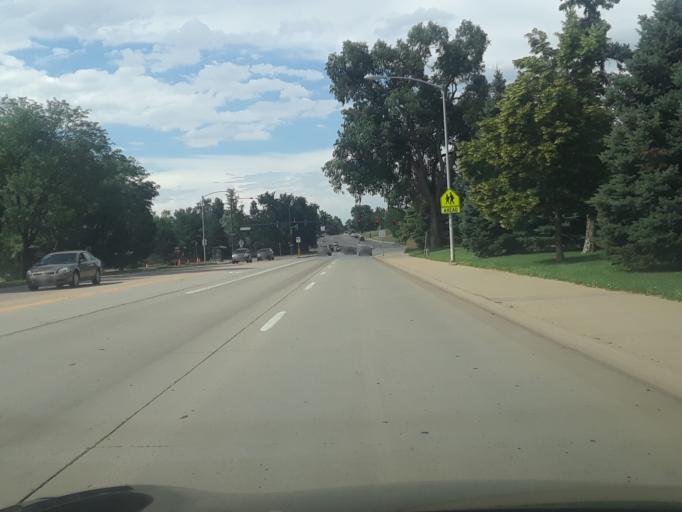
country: US
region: Colorado
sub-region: Arapahoe County
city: Glendale
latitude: 39.7240
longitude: -104.9034
